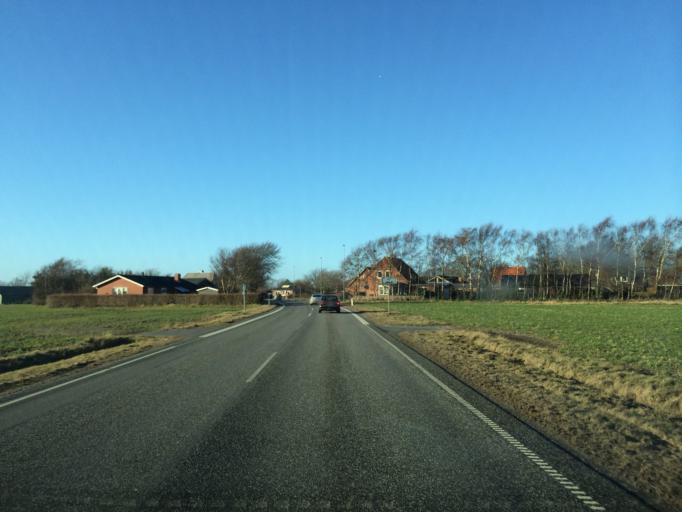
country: DK
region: Central Jutland
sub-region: Ringkobing-Skjern Kommune
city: Ringkobing
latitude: 56.1091
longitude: 8.3198
